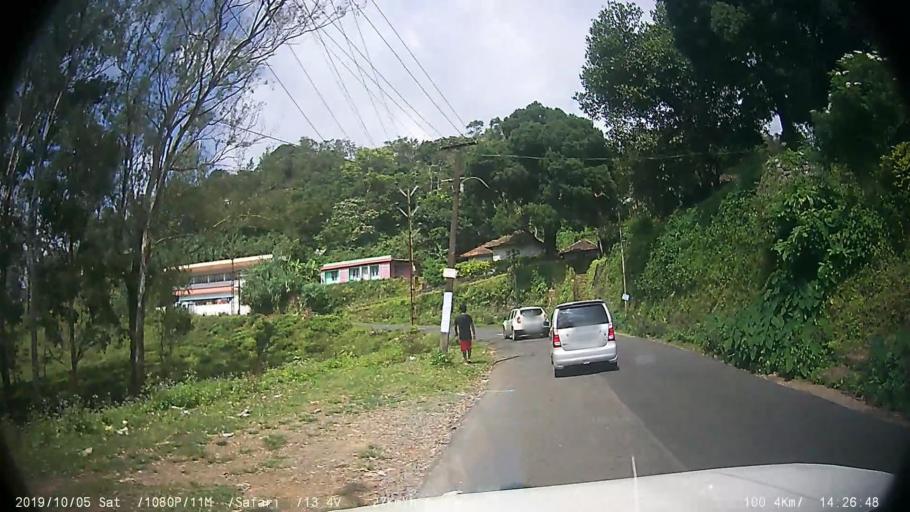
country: IN
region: Kerala
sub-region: Kottayam
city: Erattupetta
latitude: 9.6005
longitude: 76.9666
